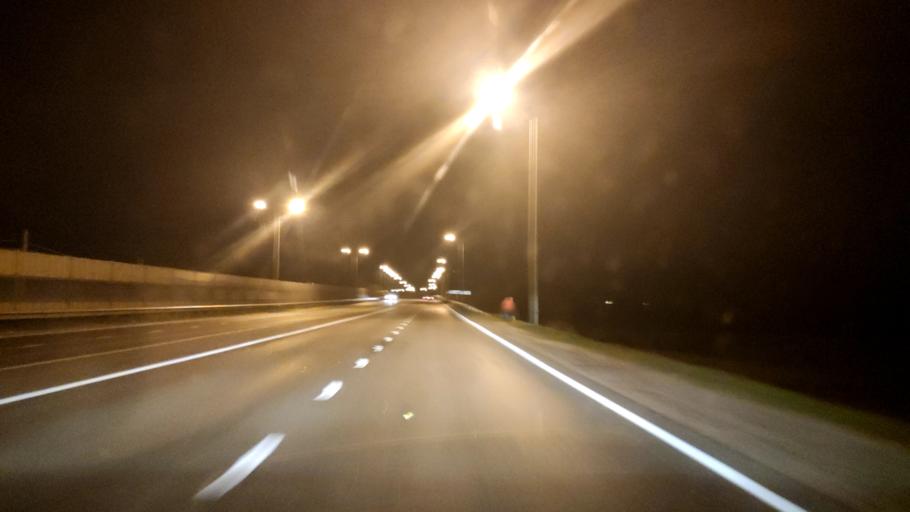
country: RU
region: Belgorod
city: Staryy Oskol
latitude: 51.3441
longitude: 37.8124
